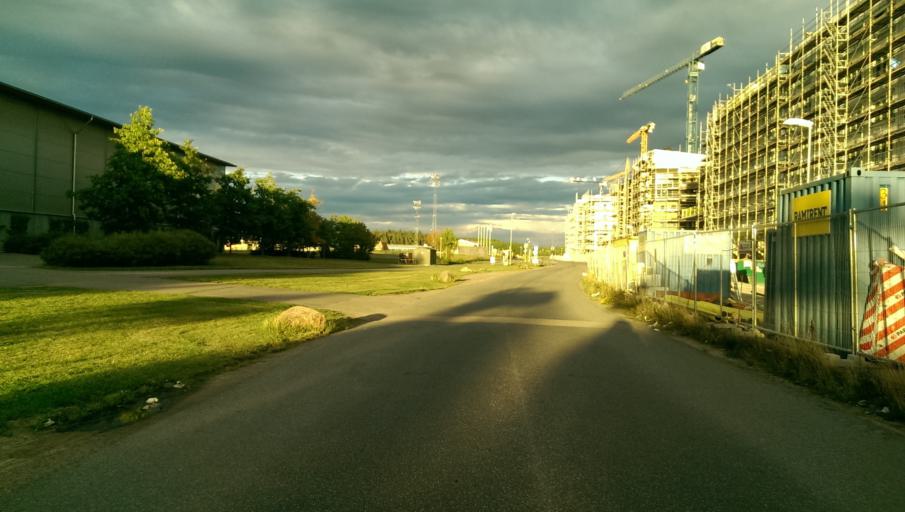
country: SE
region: OEstergoetland
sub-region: Linkopings Kommun
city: Linkoping
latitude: 58.3938
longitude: 15.5786
